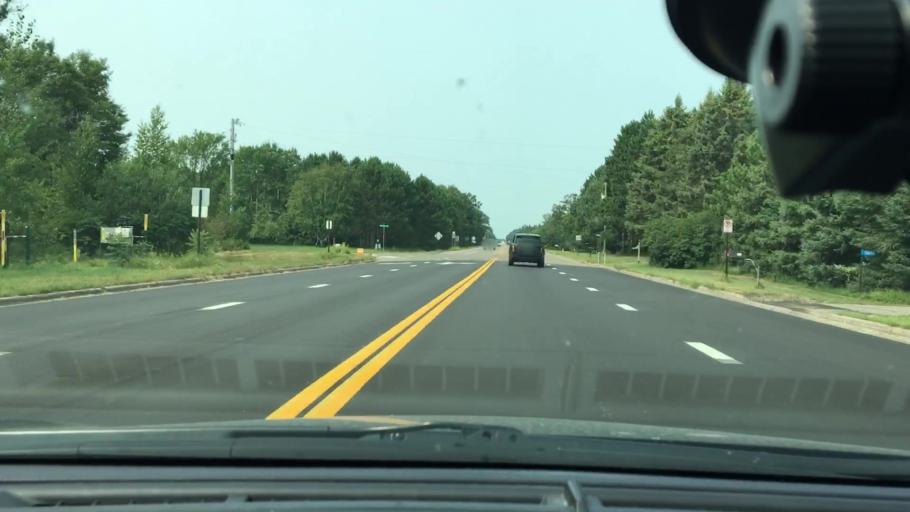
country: US
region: Minnesota
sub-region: Crow Wing County
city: Brainerd
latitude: 46.3987
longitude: -94.1776
